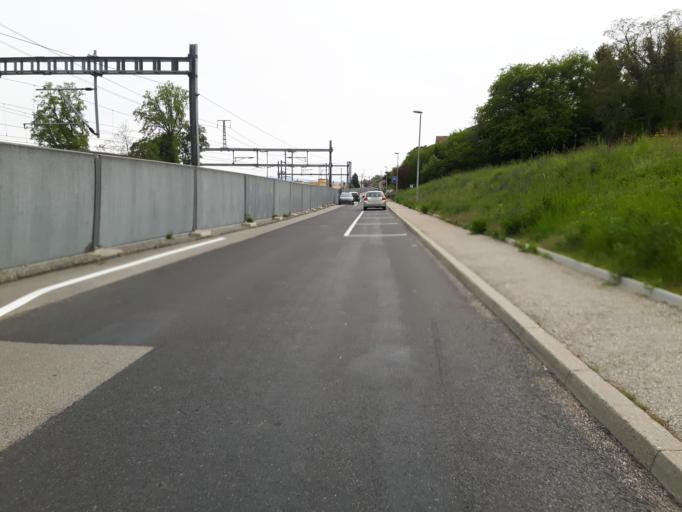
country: CH
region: Neuchatel
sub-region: Boudry District
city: Bevaix
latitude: 46.9297
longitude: 6.8113
